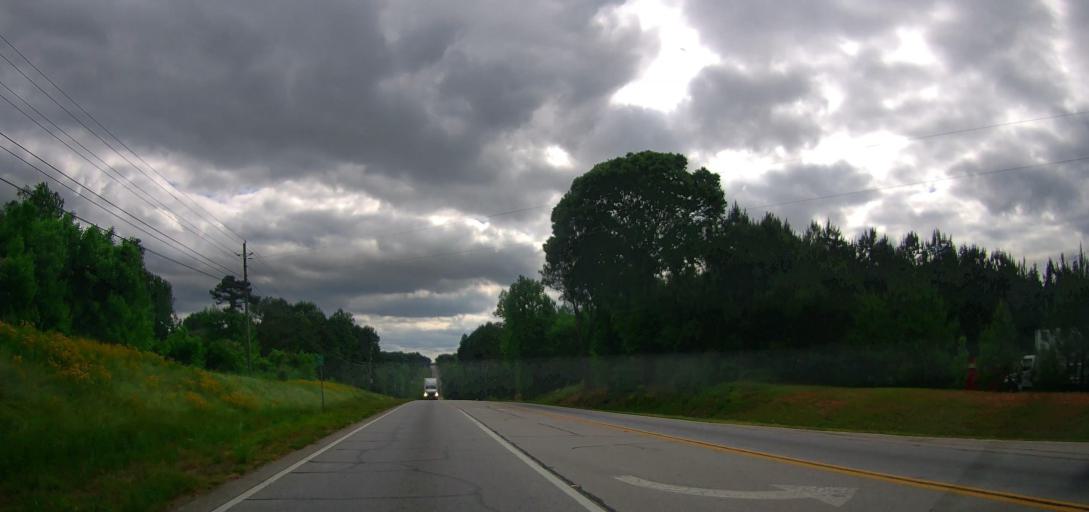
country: US
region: Georgia
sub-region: Walton County
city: Walnut Grove
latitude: 33.7697
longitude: -83.7984
